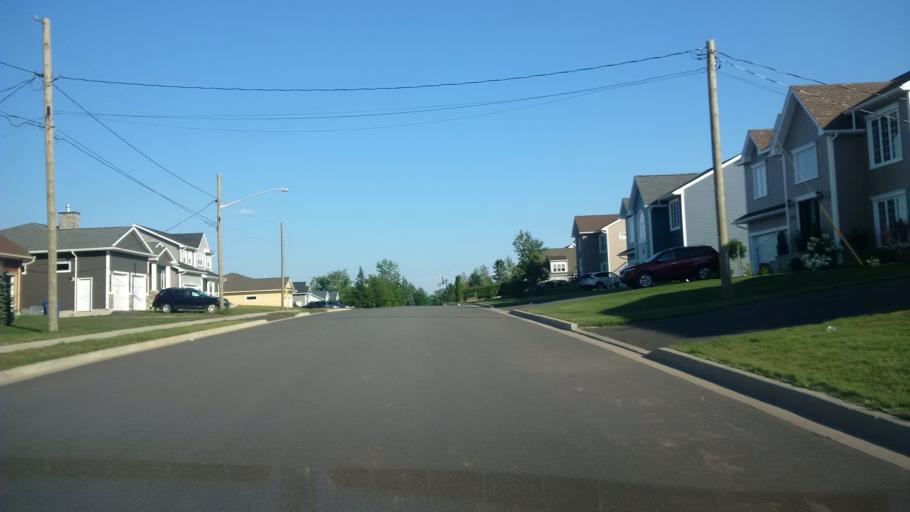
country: CA
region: New Brunswick
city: Fredericton
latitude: 45.9003
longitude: -66.6940
